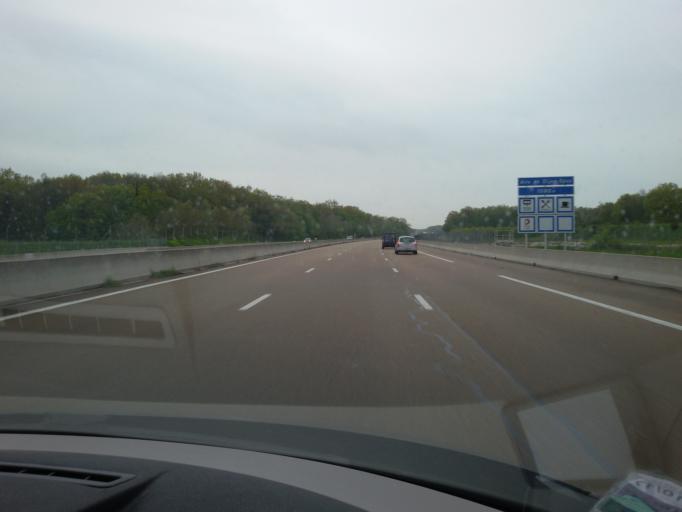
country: FR
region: Bourgogne
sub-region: Departement de la Cote-d'Or
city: Saint-Julien
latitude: 47.4103
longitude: 5.1790
